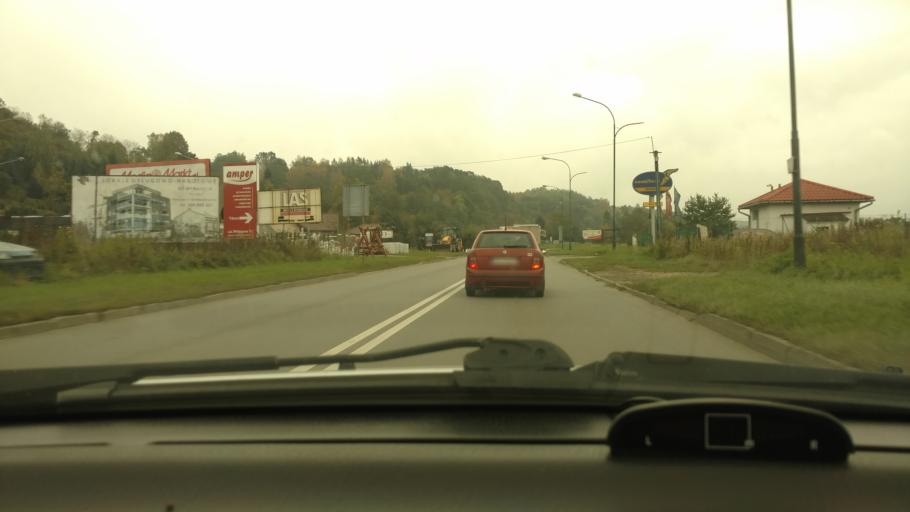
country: PL
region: Lesser Poland Voivodeship
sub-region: Powiat nowosadecki
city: Nowy Sacz
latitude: 49.6374
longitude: 20.6988
